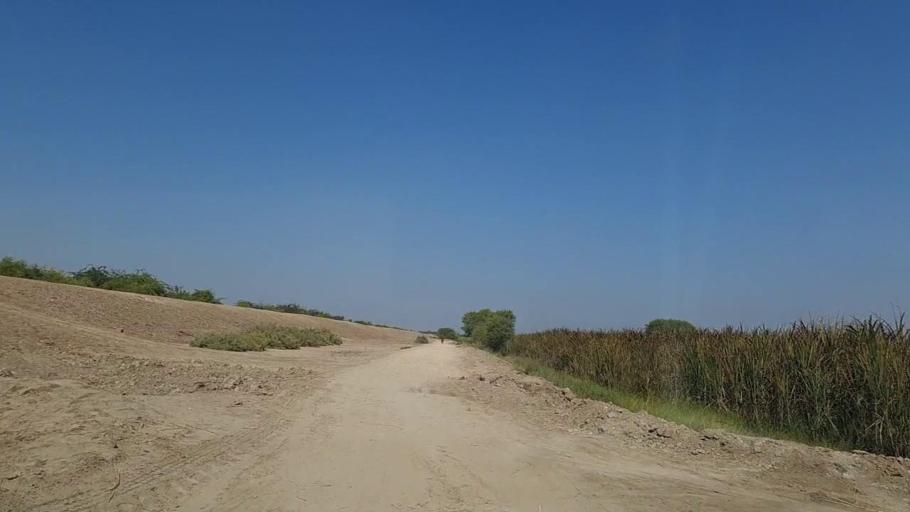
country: PK
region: Sindh
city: Chuhar Jamali
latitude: 24.4814
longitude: 68.0131
